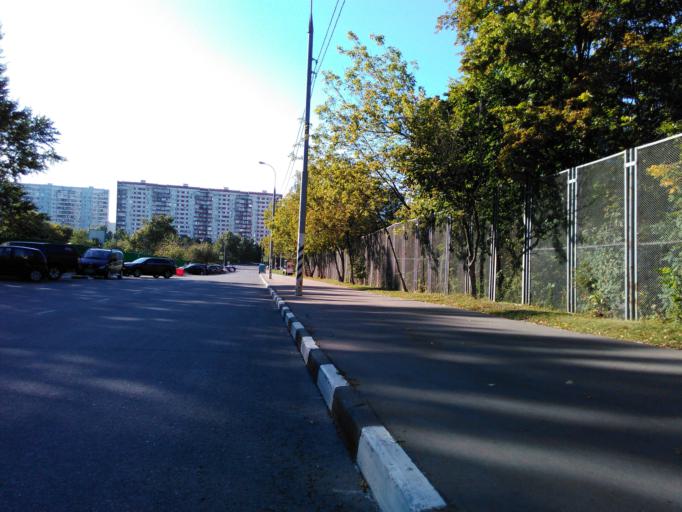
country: RU
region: Moscow
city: Troparevo
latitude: 55.6516
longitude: 37.4938
